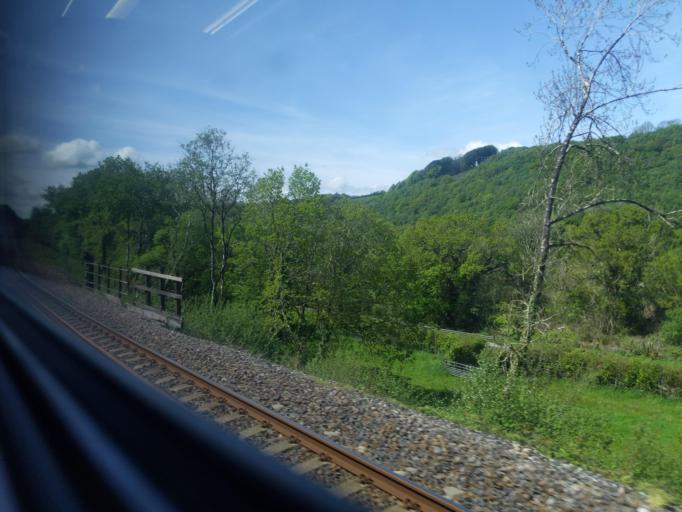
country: GB
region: England
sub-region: Cornwall
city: Lostwithiel
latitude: 50.4566
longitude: -4.6200
